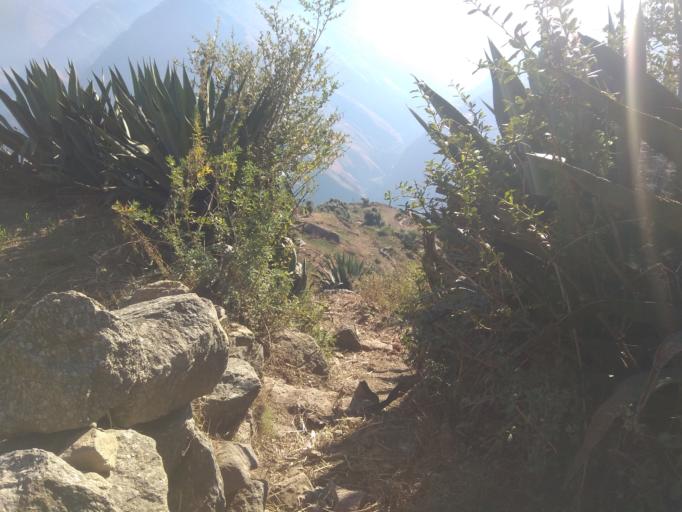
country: NP
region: Mid Western
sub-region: Karnali Zone
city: Jumla
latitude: 29.3138
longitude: 81.7381
